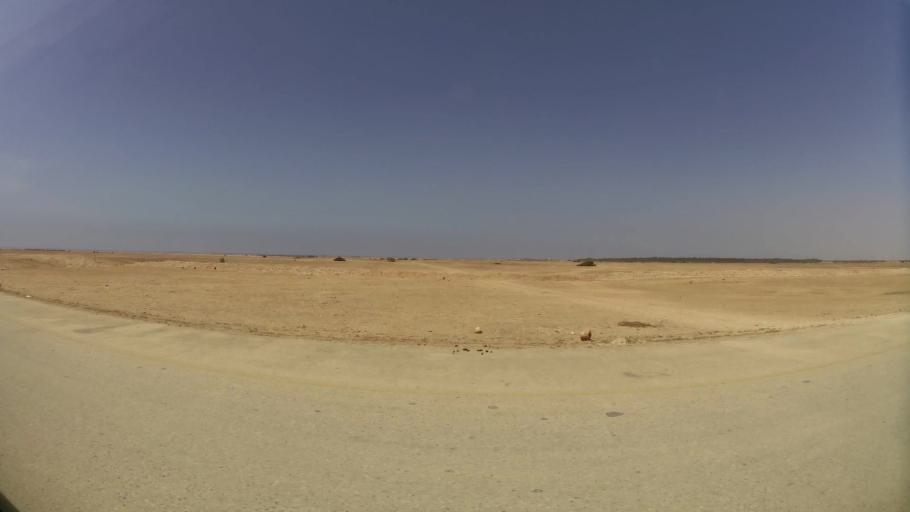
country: OM
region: Zufar
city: Salalah
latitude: 17.0478
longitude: 54.2404
